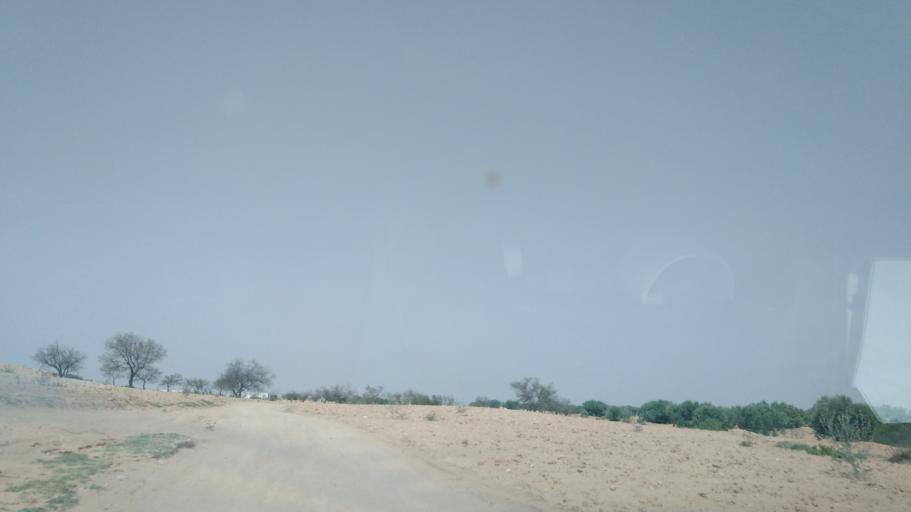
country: TN
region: Safaqis
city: Sfax
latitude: 34.6393
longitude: 10.5668
